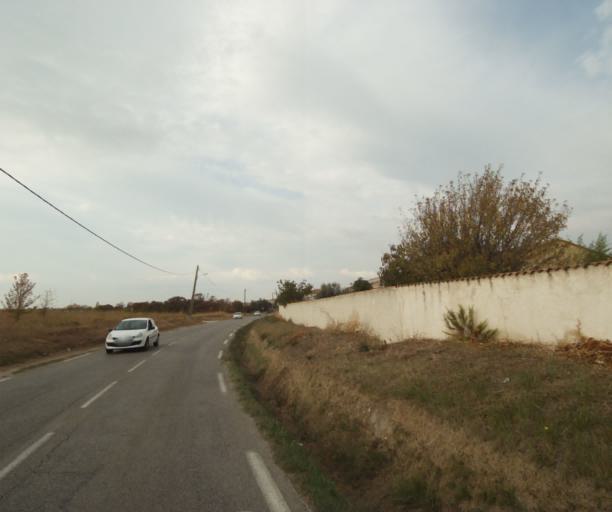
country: FR
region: Provence-Alpes-Cote d'Azur
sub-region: Departement des Bouches-du-Rhone
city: Marignane
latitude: 43.4011
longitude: 5.2167
